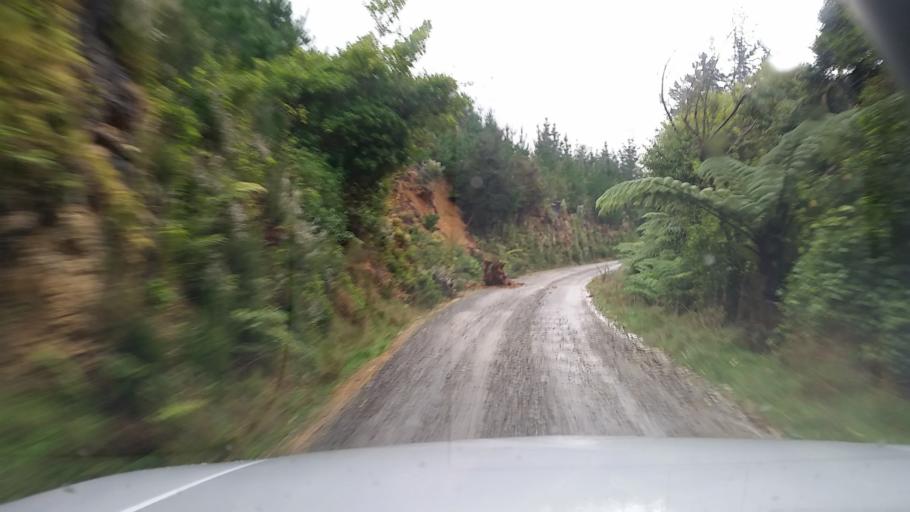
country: NZ
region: Marlborough
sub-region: Marlborough District
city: Picton
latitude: -41.1331
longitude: 174.0402
